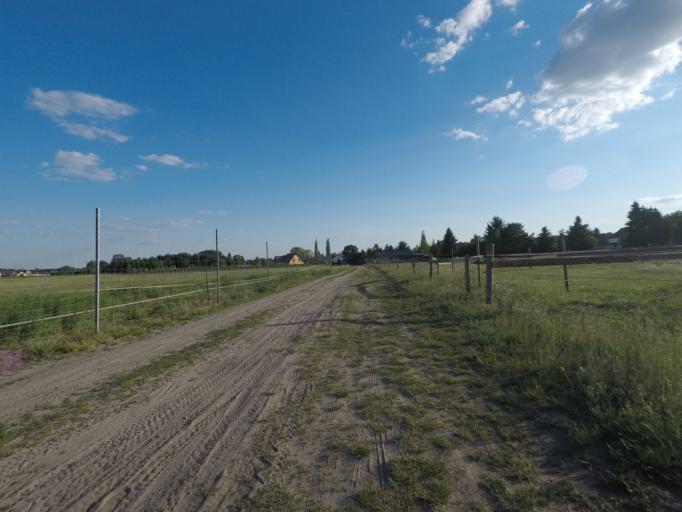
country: DE
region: Brandenburg
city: Melchow
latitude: 52.8580
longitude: 13.6847
